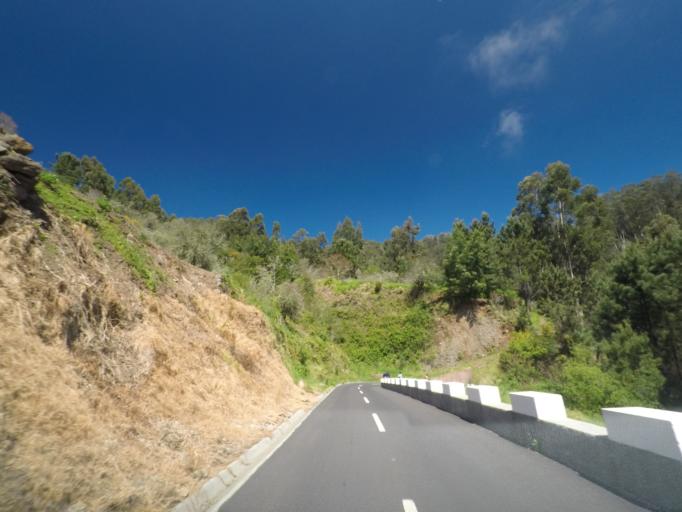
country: PT
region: Madeira
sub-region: Calheta
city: Arco da Calheta
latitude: 32.7289
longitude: -17.1217
